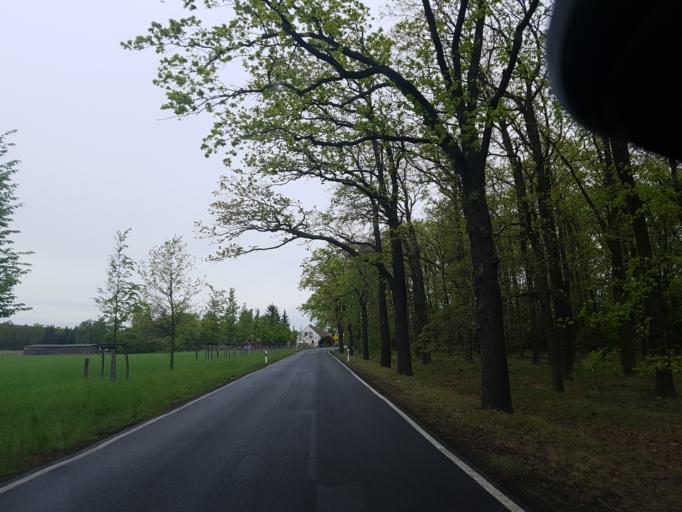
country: DE
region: Brandenburg
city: Spremberg
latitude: 51.6414
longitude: 14.4331
